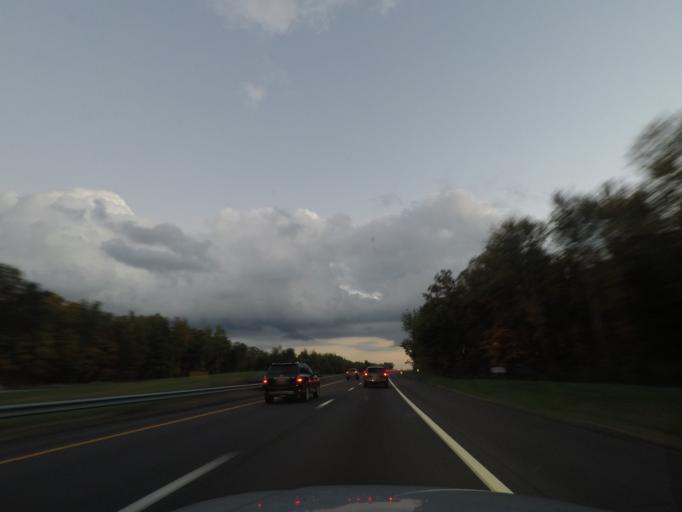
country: US
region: New York
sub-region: Ulster County
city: Plattekill
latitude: 41.6491
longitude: -74.0771
